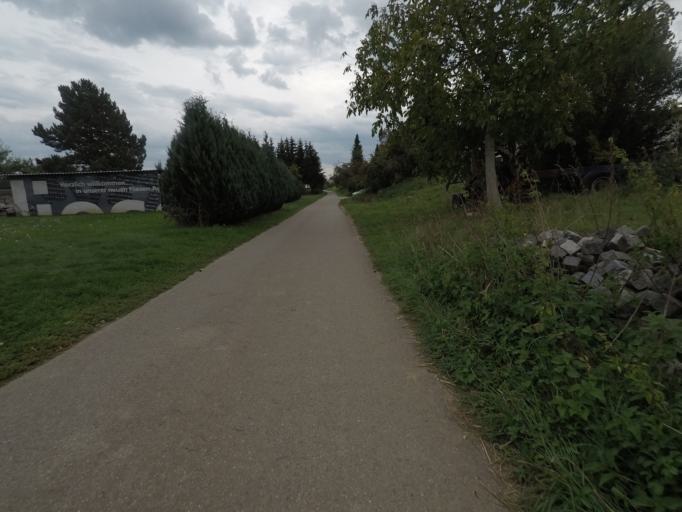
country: DE
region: Baden-Wuerttemberg
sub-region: Regierungsbezirk Stuttgart
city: Herrenberg
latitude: 48.5620
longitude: 8.8995
